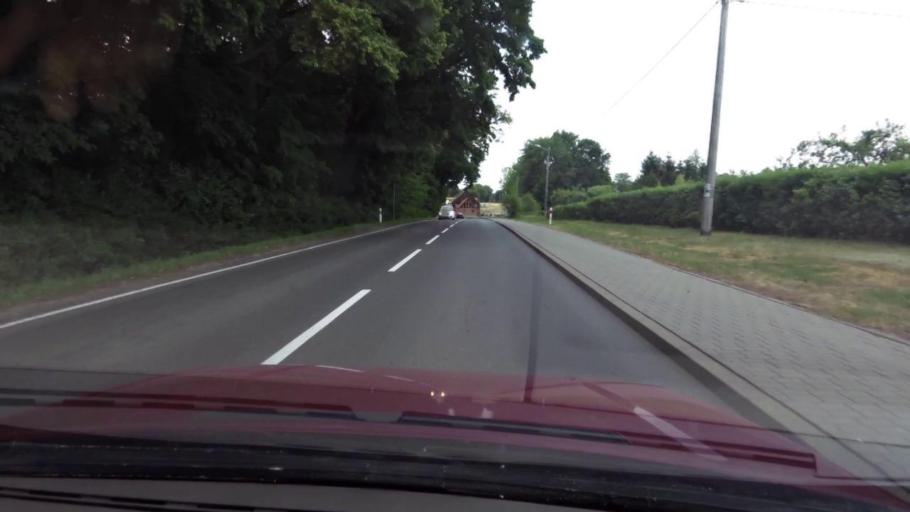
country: PL
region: Pomeranian Voivodeship
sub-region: Powiat bytowski
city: Trzebielino
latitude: 54.2068
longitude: 17.0898
